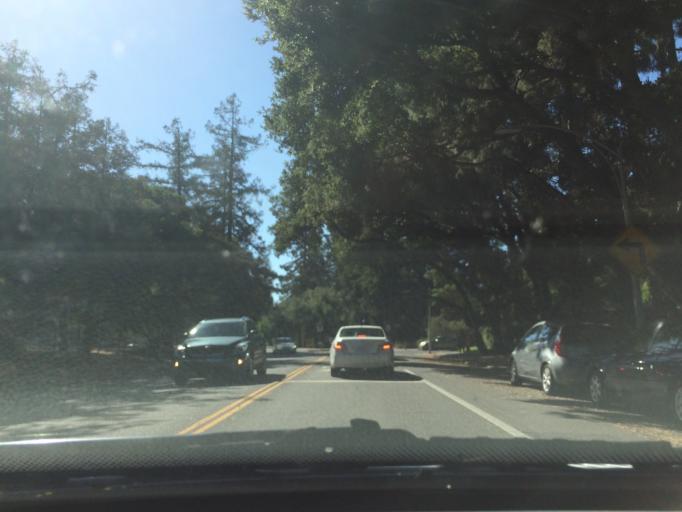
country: US
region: California
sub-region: San Mateo County
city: Menlo Park
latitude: 37.4463
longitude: -122.1685
